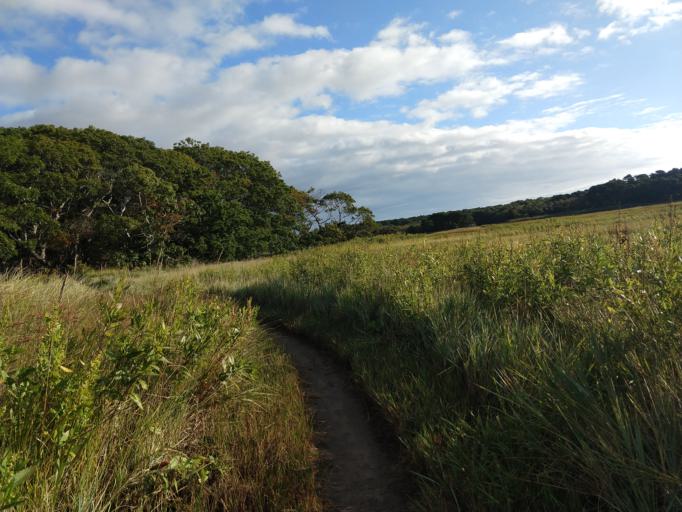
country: US
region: Massachusetts
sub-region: Barnstable County
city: North Eastham
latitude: 41.8819
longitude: -70.0007
